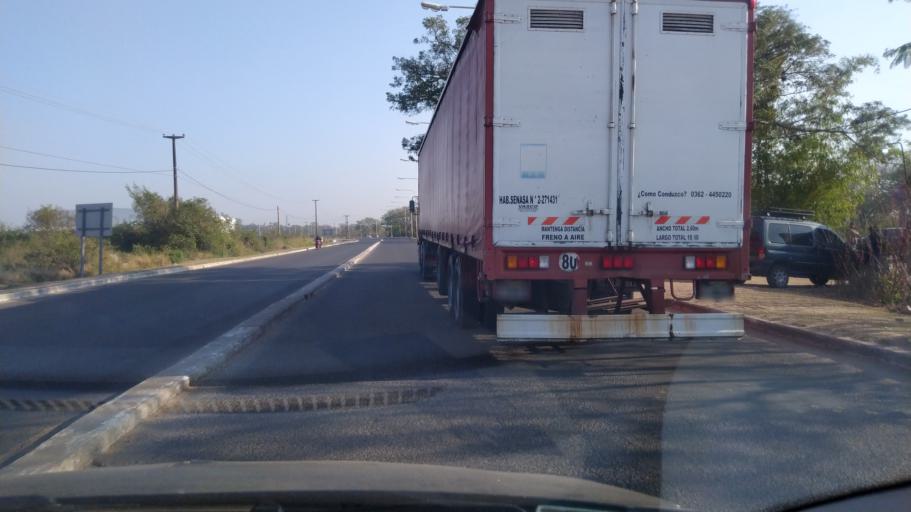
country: AR
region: Corrientes
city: Corrientes
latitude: -27.5210
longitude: -58.8003
